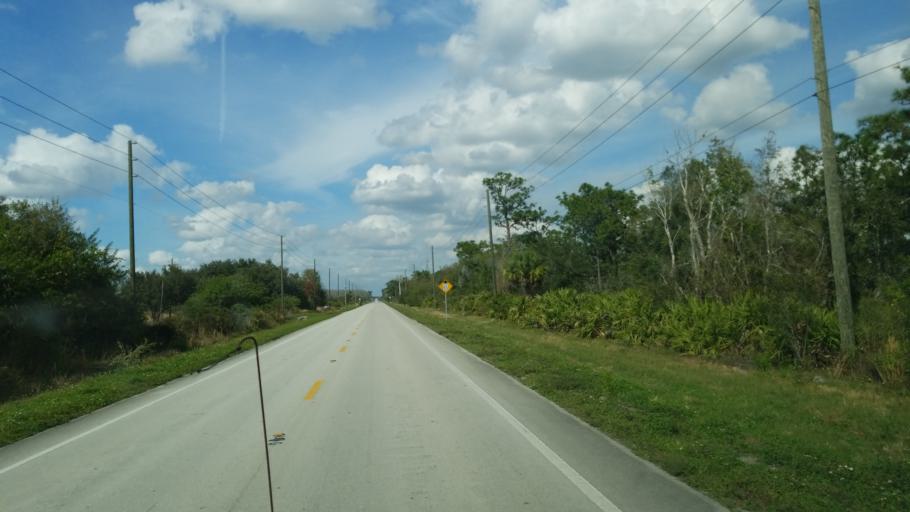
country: US
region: Florida
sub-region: Osceola County
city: Saint Cloud
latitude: 28.1204
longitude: -81.0763
